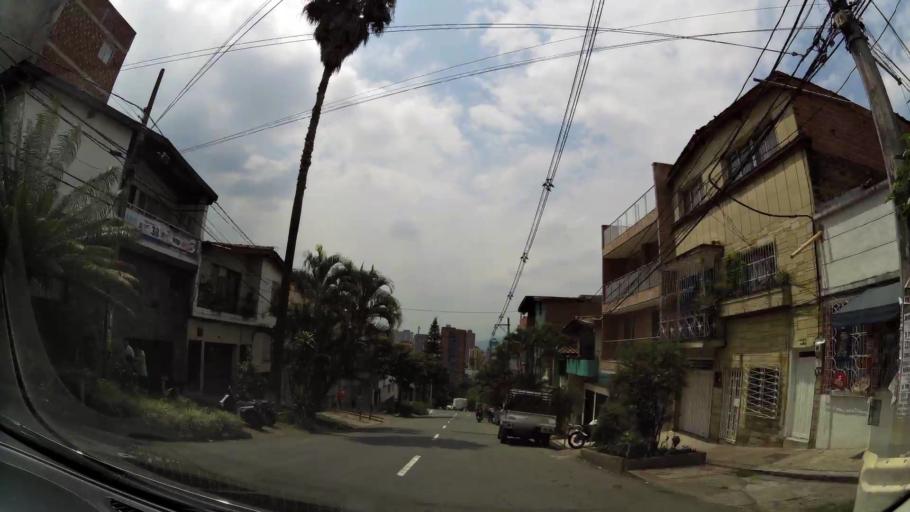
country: CO
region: Antioquia
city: Medellin
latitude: 6.2550
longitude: -75.5583
